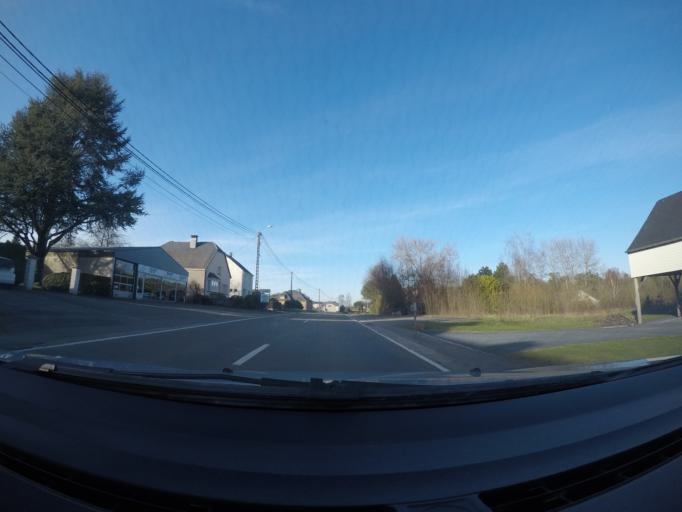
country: BE
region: Wallonia
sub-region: Province du Luxembourg
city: Tintigny
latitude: 49.6707
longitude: 5.5028
